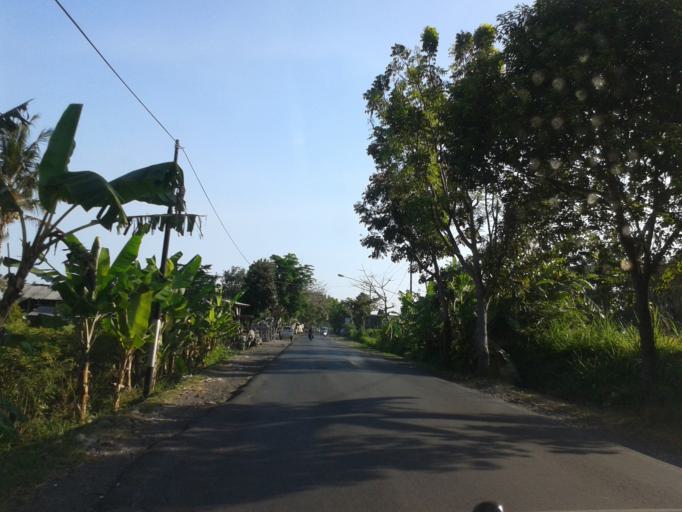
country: ID
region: Bali
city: Banjar Wangsian
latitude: -8.5043
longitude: 115.4036
